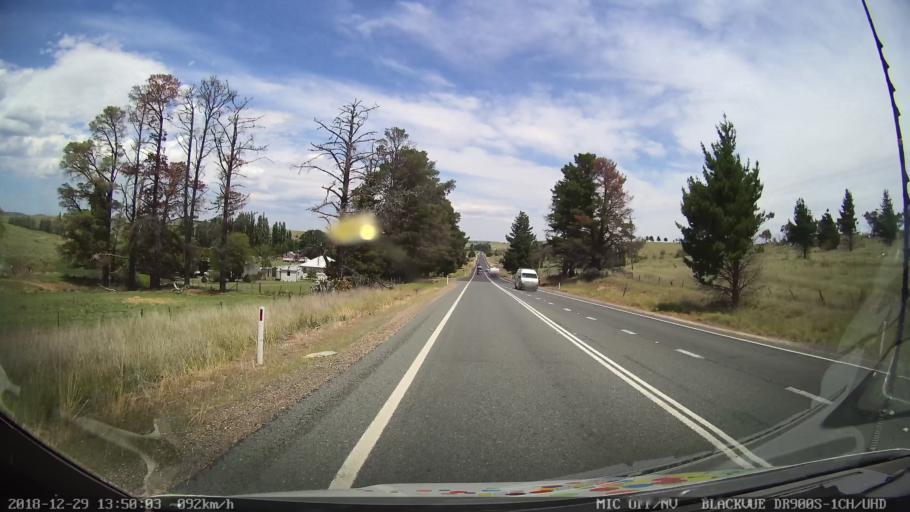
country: AU
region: New South Wales
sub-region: Cooma-Monaro
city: Cooma
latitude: -36.1624
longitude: 149.1530
